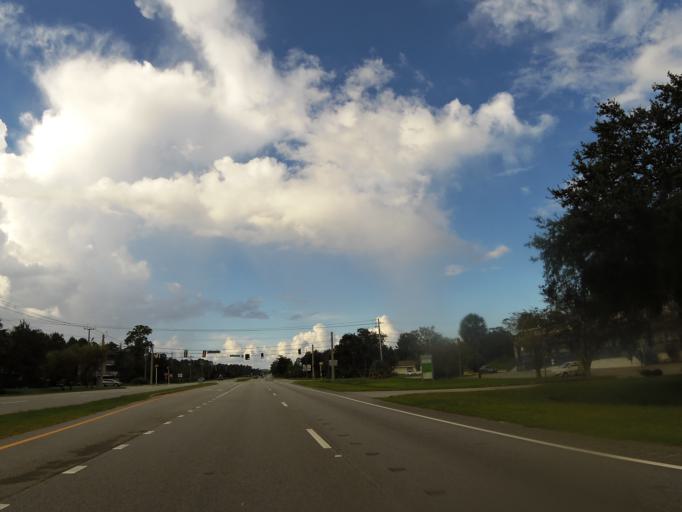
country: US
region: Georgia
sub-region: Glynn County
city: Country Club Estates
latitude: 31.1912
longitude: -81.4691
